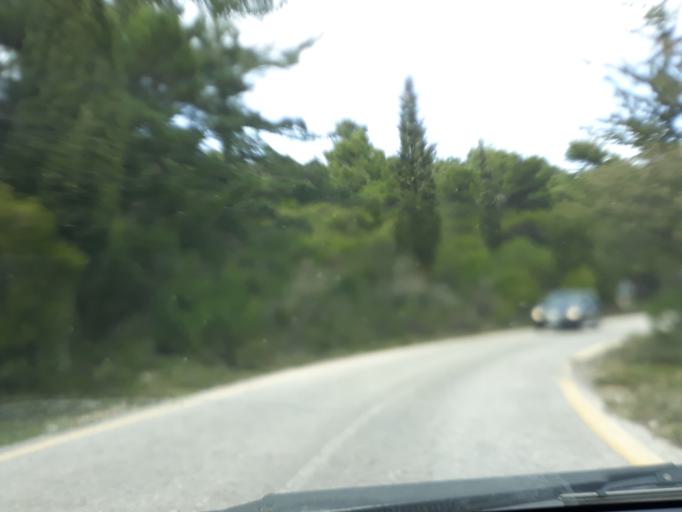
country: GR
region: Attica
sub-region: Nomarchia Anatolikis Attikis
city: Afidnes
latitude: 38.1806
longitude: 23.7914
